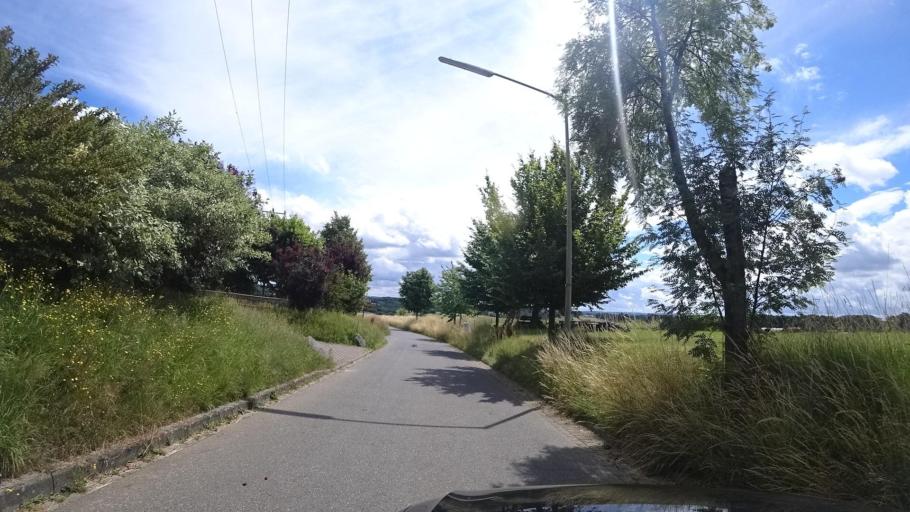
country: DE
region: Rheinland-Pfalz
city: Seifen
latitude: 50.6700
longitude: 7.5159
